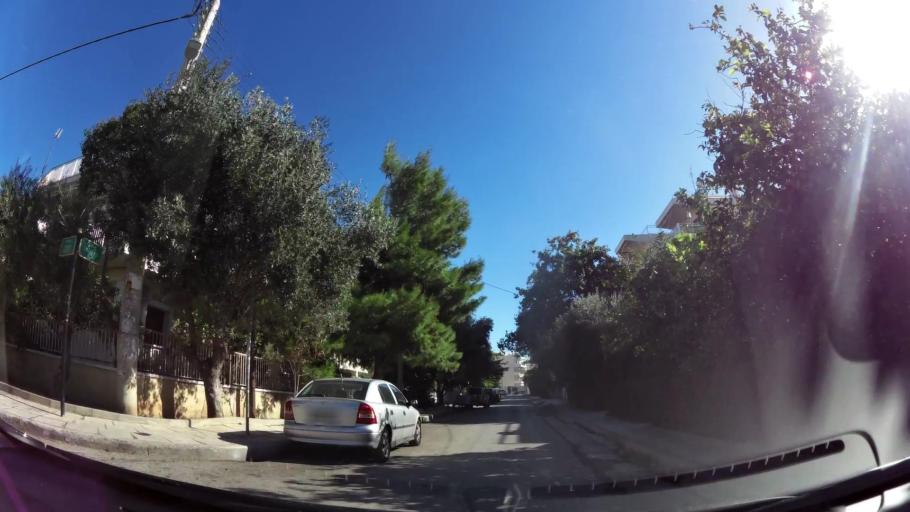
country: GR
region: Attica
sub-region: Nomarchia Athinas
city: Glyfada
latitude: 37.8509
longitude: 23.7604
